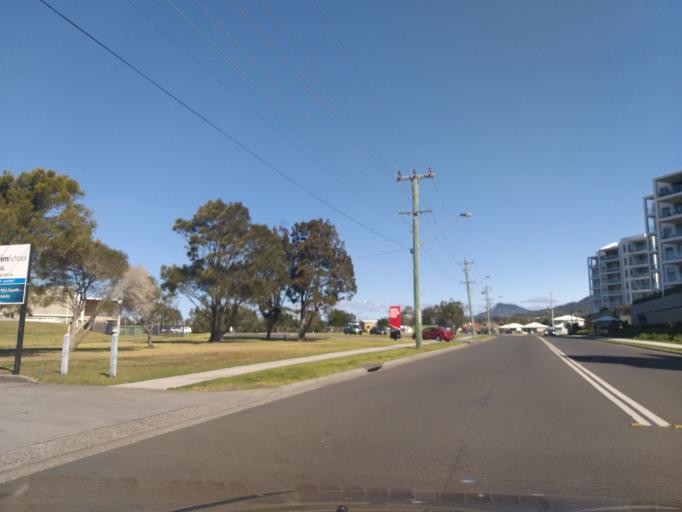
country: AU
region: New South Wales
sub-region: Wollongong
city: Fairy Meadow
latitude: -34.3902
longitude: 150.9043
